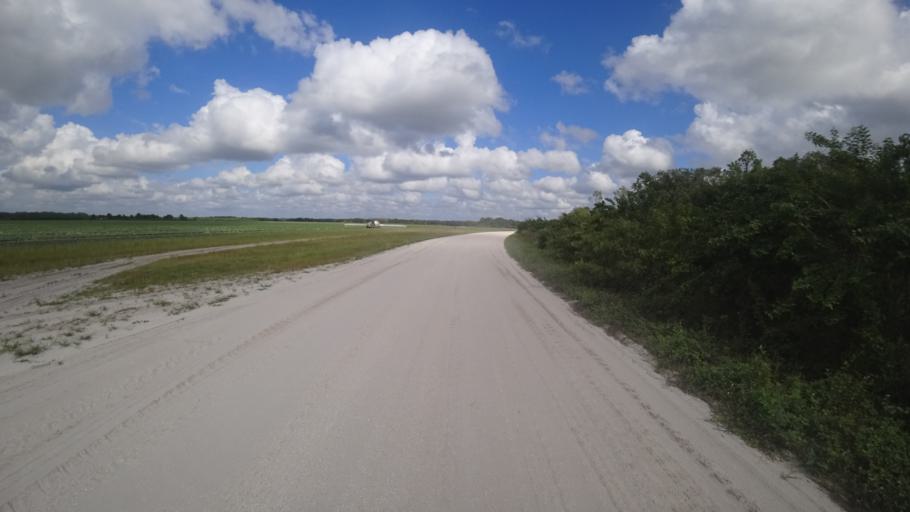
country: US
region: Florida
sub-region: Sarasota County
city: Lake Sarasota
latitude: 27.4169
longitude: -82.1888
